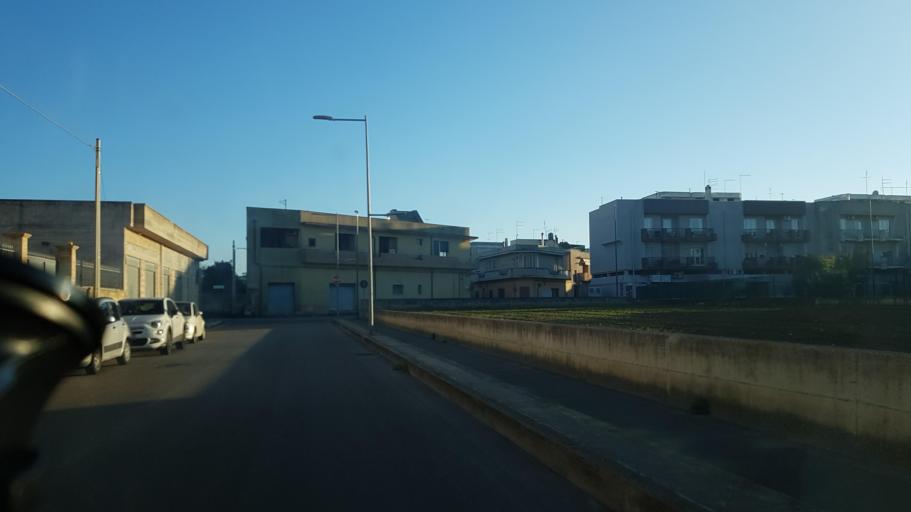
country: IT
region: Apulia
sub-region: Provincia di Brindisi
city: Latiano
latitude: 40.5553
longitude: 17.7242
